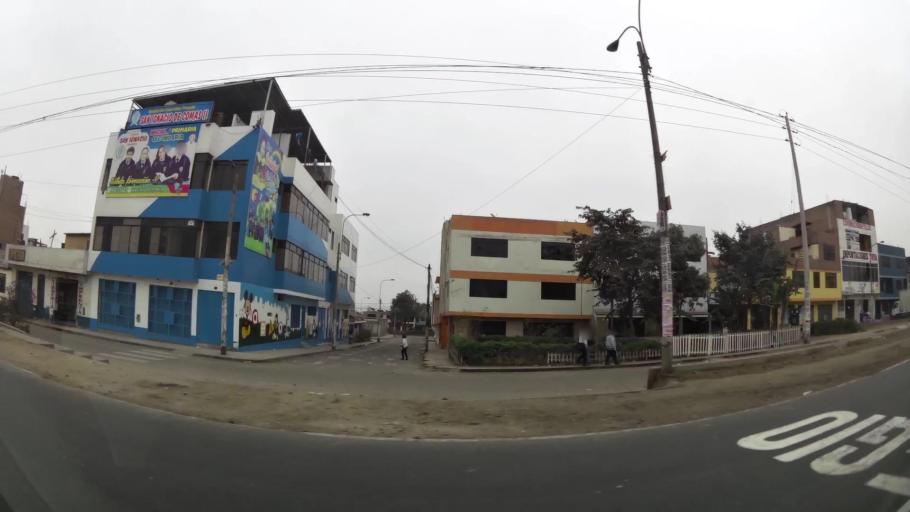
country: PE
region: Lima
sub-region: Lima
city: Urb. Santo Domingo
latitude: -11.9204
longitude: -77.0424
